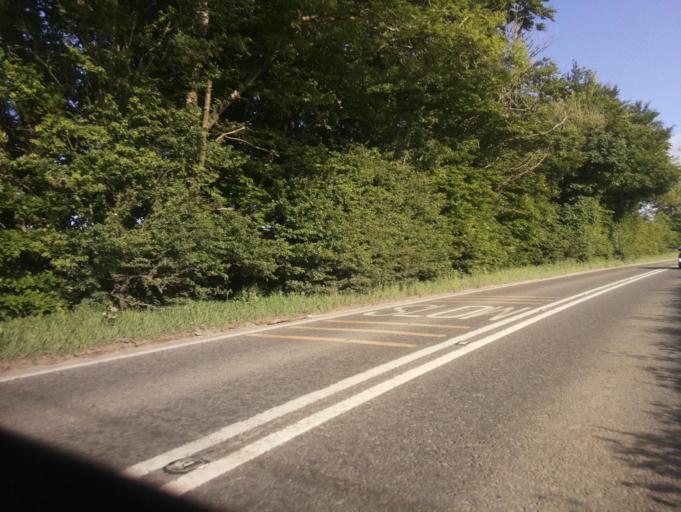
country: GB
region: England
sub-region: Somerset
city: Shepton Mallet
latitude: 51.2181
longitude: -2.5313
